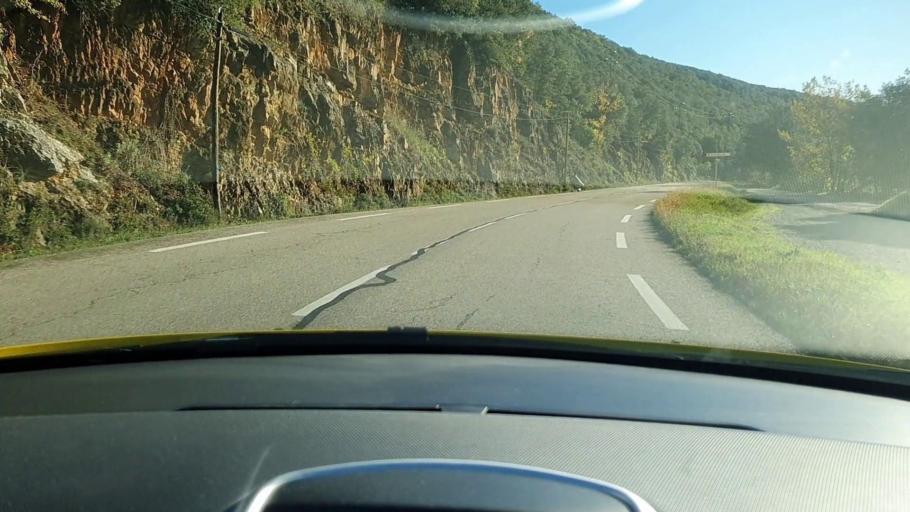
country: FR
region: Languedoc-Roussillon
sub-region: Departement du Gard
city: Saint-Hippolyte-du-Fort
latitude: 43.9892
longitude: 3.8525
